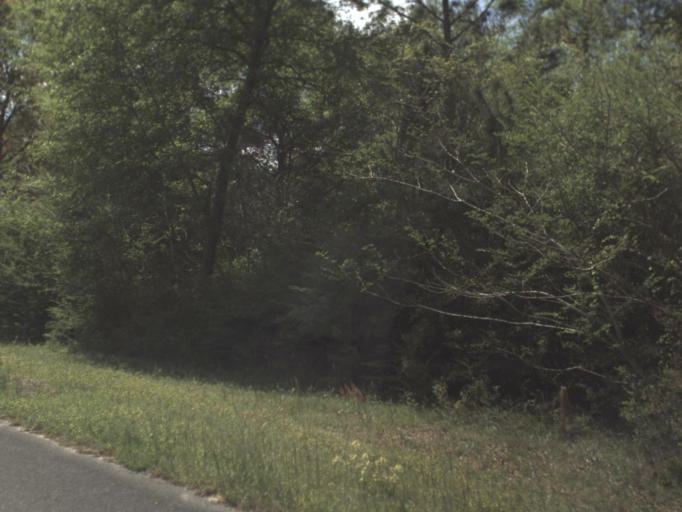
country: US
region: Florida
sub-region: Okaloosa County
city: Crestview
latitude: 30.8566
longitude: -86.6747
